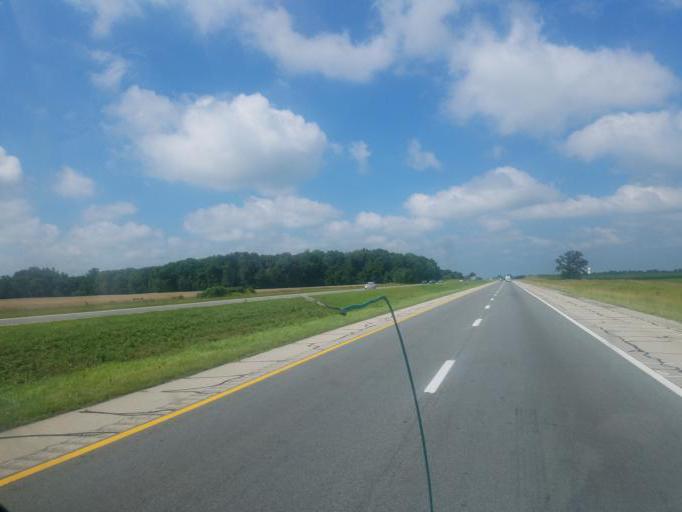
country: US
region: Ohio
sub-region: Madison County
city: Bethel
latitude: 39.7081
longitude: -83.4276
